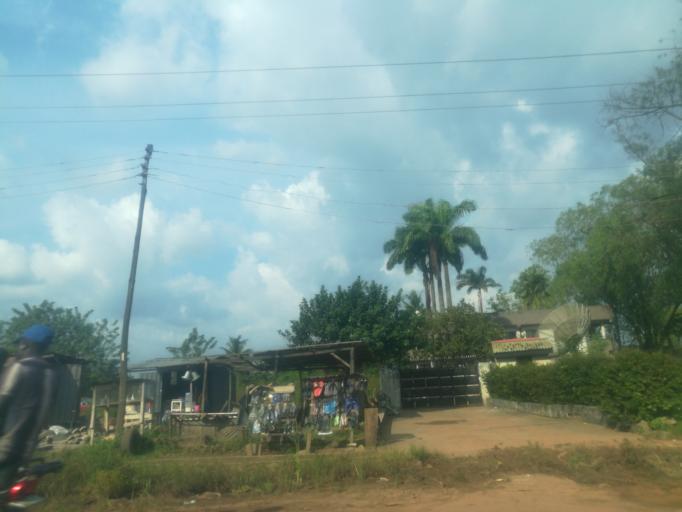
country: NG
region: Oyo
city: Ibadan
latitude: 7.3919
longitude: 3.8148
